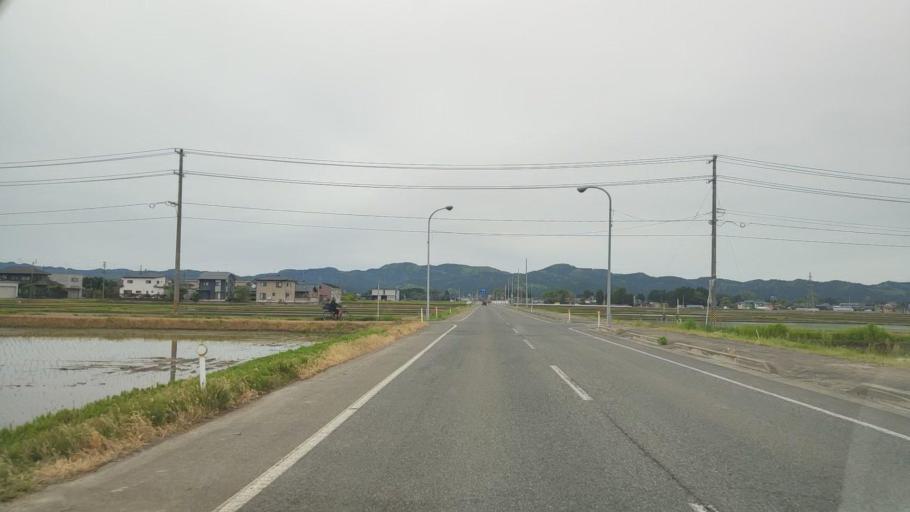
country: JP
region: Niigata
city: Gosen
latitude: 37.7292
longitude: 139.1712
